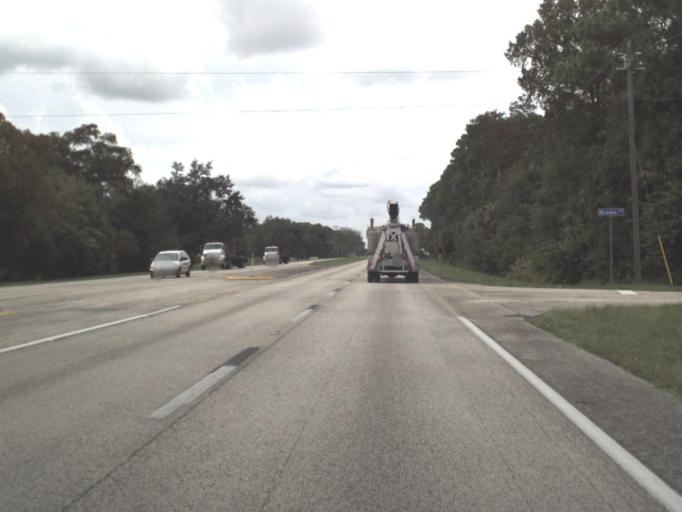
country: US
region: Florida
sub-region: Lee County
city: Olga
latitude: 26.7142
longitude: -81.6999
